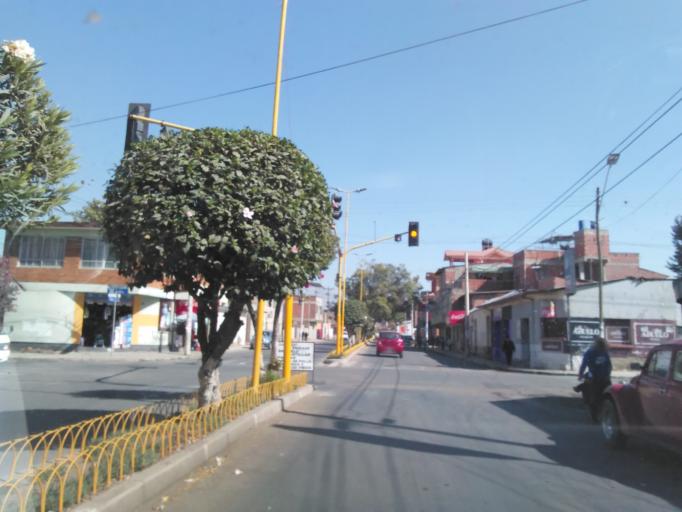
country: BO
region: Cochabamba
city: Sipe Sipe
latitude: -17.3981
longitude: -66.2766
